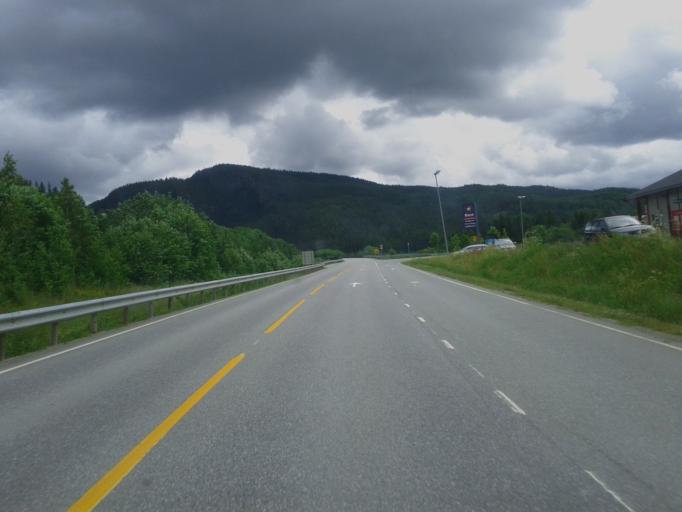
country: NO
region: Sor-Trondelag
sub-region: Midtre Gauldal
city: Storen
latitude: 62.9429
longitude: 10.6537
